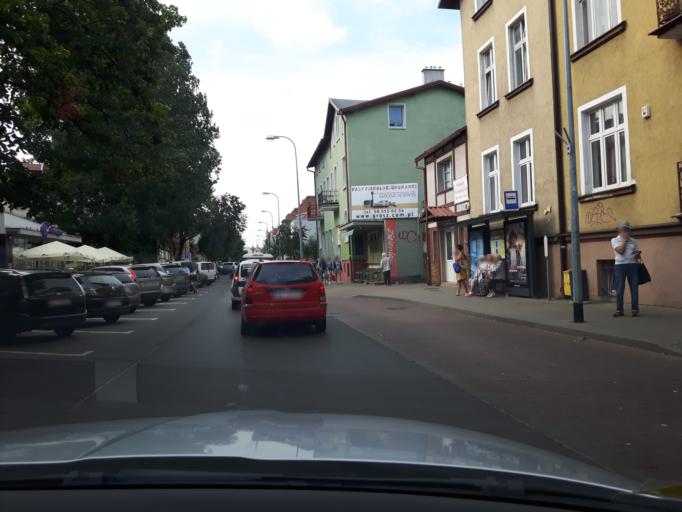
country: PL
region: Pomeranian Voivodeship
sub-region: Sopot
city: Sopot
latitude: 54.4390
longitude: 18.5738
